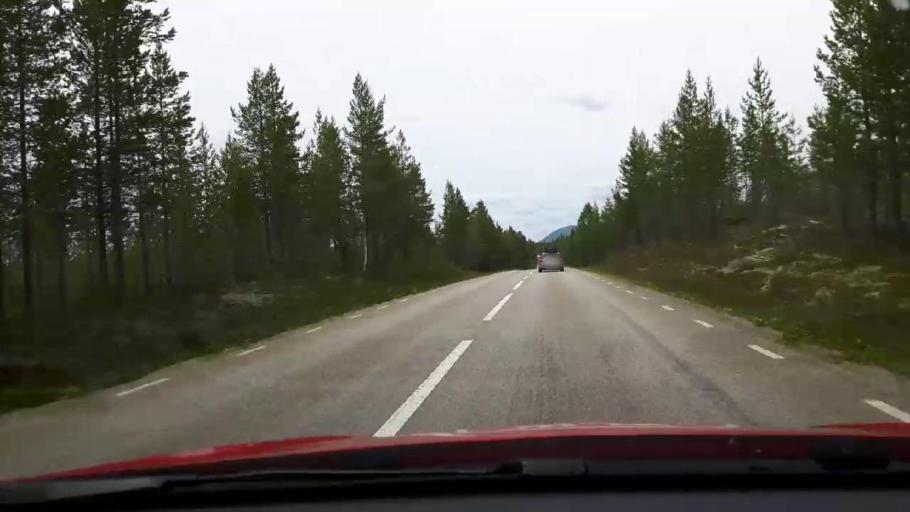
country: SE
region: Jaemtland
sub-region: Harjedalens Kommun
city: Sveg
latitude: 62.2306
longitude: 13.8571
